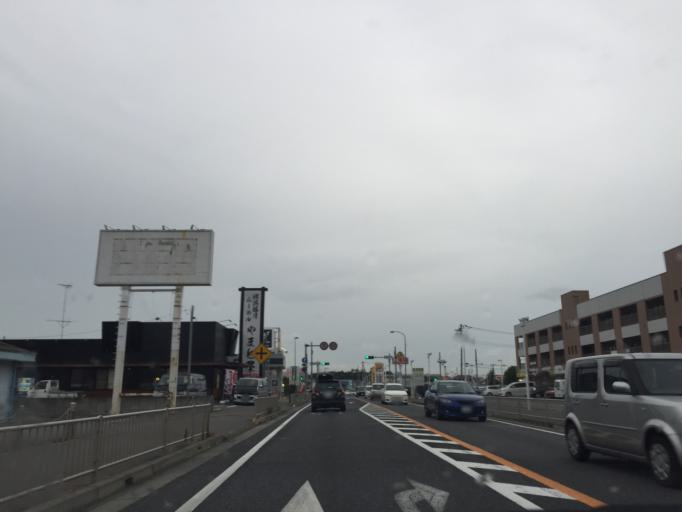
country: JP
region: Ibaraki
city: Naka
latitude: 36.0115
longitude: 140.1562
